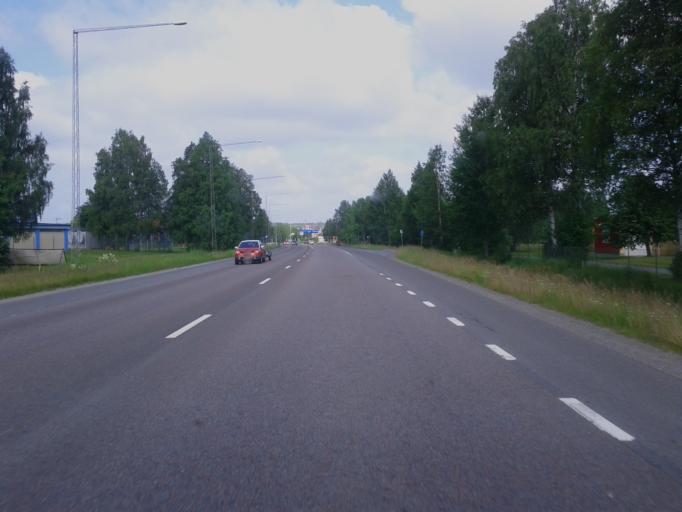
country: SE
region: Vaesterbotten
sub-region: Skelleftea Kommun
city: Skelleftea
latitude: 64.7399
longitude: 20.9638
